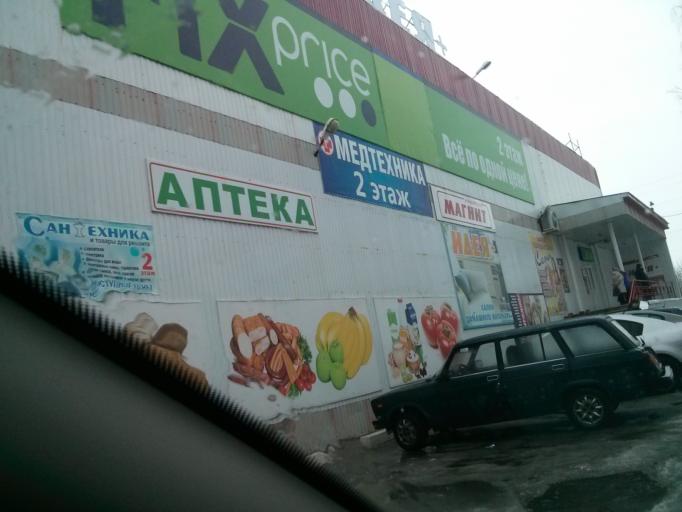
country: RU
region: Vladimir
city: Murom
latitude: 55.5505
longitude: 42.0501
